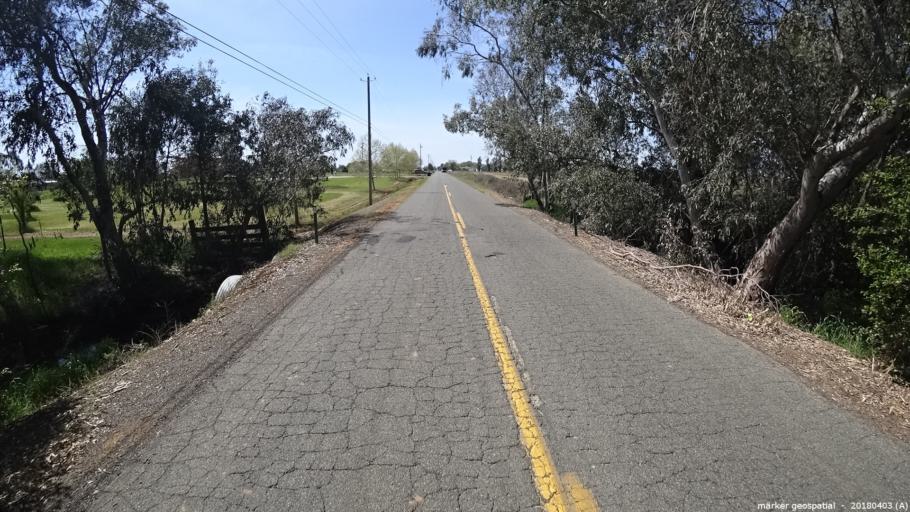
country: US
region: California
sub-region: Sacramento County
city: Herald
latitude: 38.3432
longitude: -121.2256
